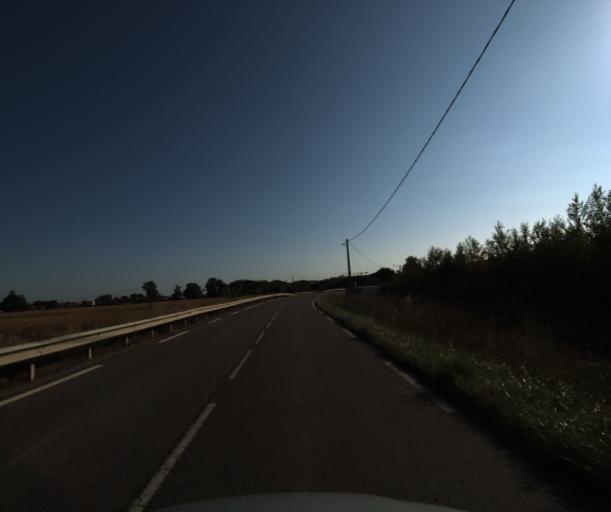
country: FR
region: Midi-Pyrenees
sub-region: Departement de la Haute-Garonne
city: Labarthe-sur-Leze
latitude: 43.4484
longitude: 1.3871
